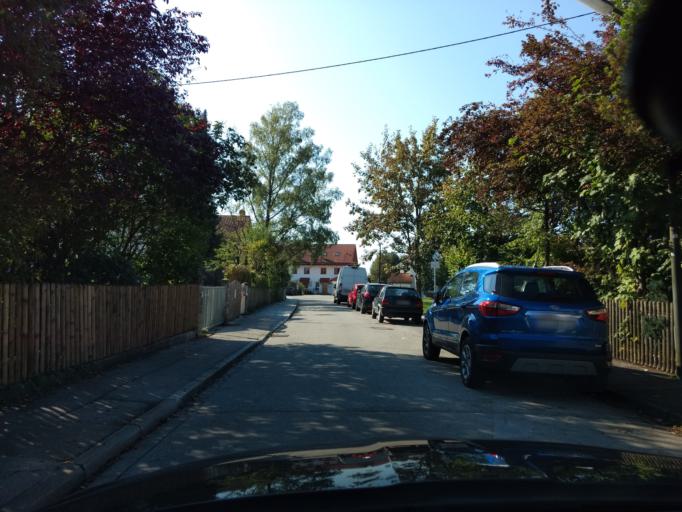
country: DE
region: Bavaria
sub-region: Upper Bavaria
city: Wolfratshausen
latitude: 47.9115
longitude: 11.4253
